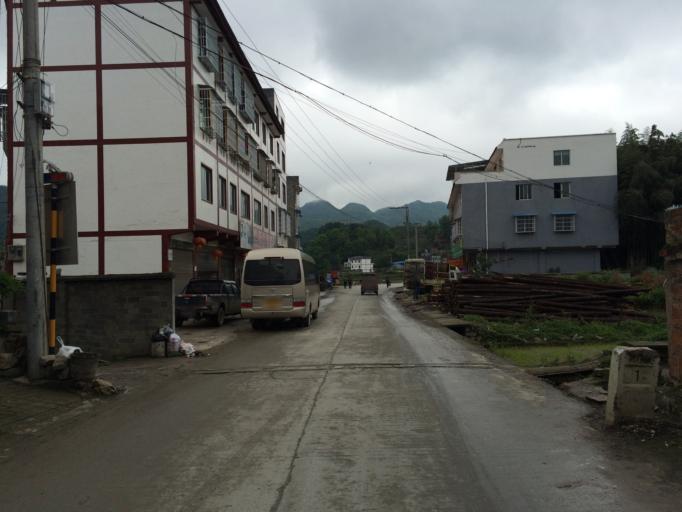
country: CN
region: Guizhou Sheng
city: Dalucao
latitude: 27.8344
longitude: 107.2539
